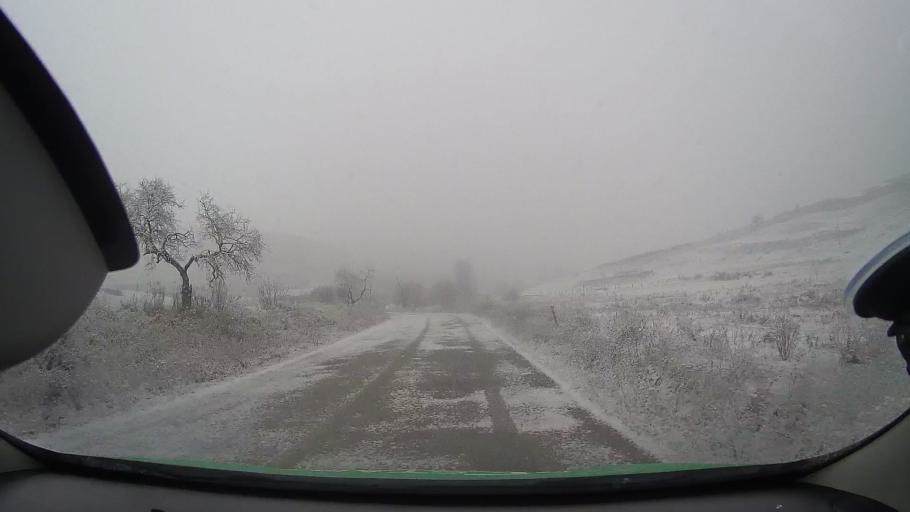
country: RO
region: Alba
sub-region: Comuna Hoparta
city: Hoparta
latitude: 46.3113
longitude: 23.8597
